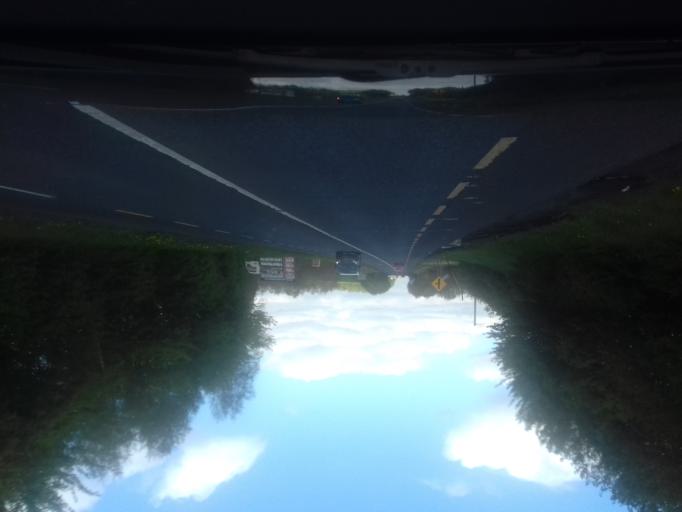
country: IE
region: Leinster
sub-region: Laois
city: Portlaoise
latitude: 53.0471
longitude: -7.2462
